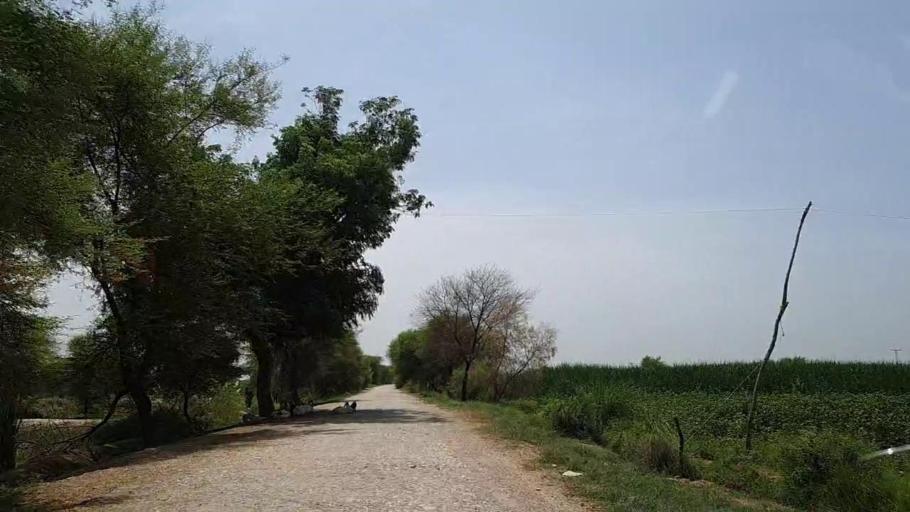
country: PK
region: Sindh
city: Khanpur
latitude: 27.8372
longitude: 69.4840
